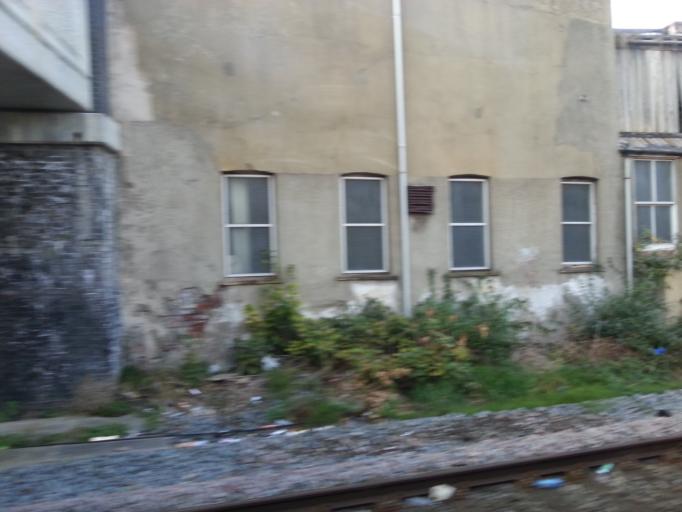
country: GB
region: England
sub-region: Sefton
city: Southport
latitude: 53.6428
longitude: -3.0015
